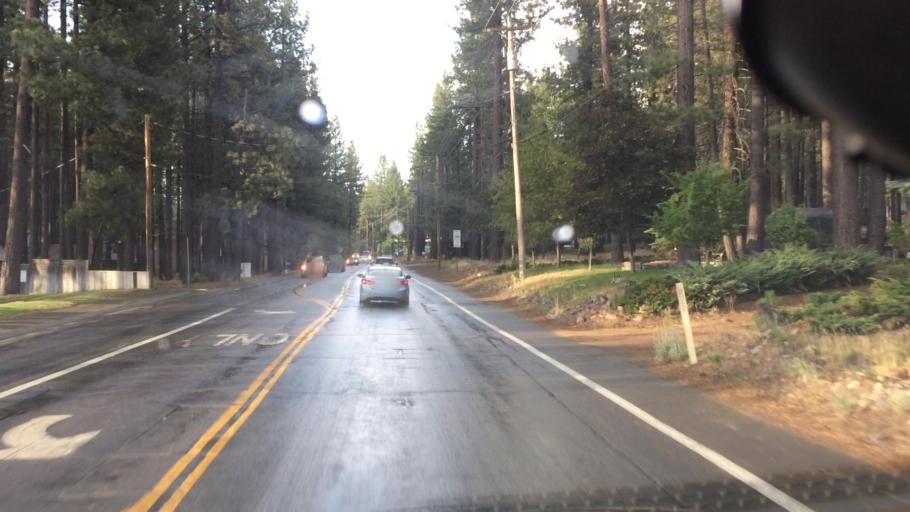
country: US
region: California
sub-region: El Dorado County
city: South Lake Tahoe
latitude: 38.9413
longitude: -119.9521
